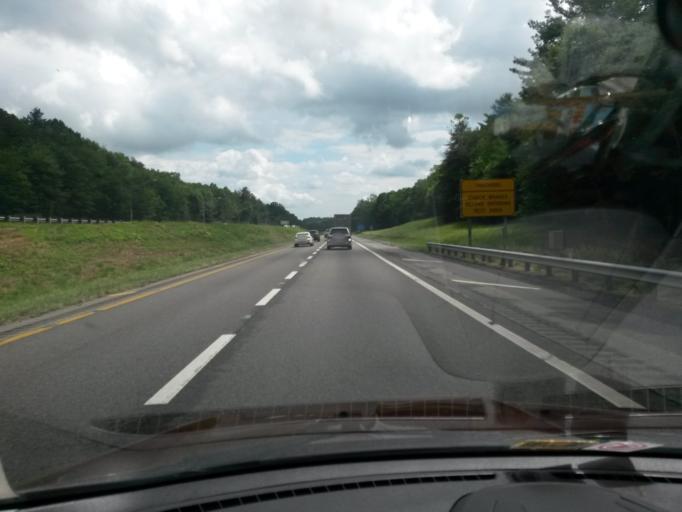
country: US
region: Virginia
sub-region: Carroll County
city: Cana
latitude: 36.5704
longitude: -80.7442
